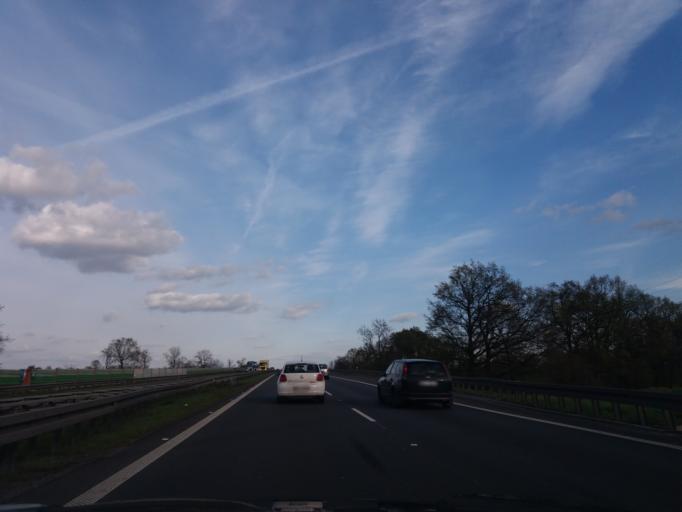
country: PL
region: Lower Silesian Voivodeship
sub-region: Powiat strzelinski
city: Wiazow
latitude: 50.8382
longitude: 17.2731
